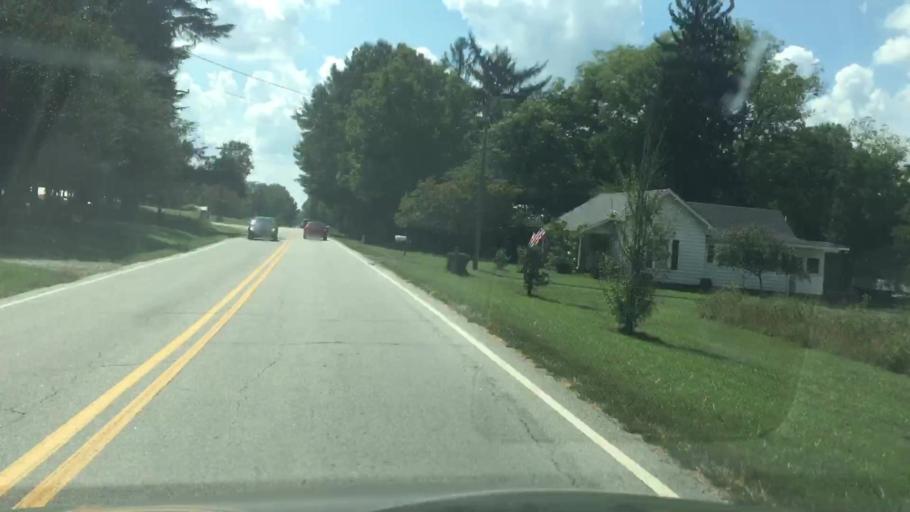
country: US
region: North Carolina
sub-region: Rowan County
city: China Grove
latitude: 35.6483
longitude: -80.6280
